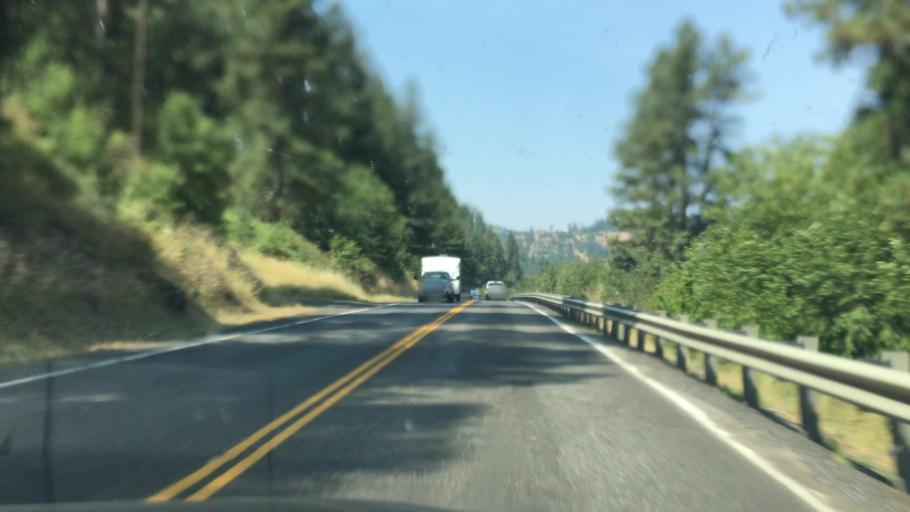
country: US
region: Idaho
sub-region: Clearwater County
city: Orofino
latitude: 46.4973
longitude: -116.4188
